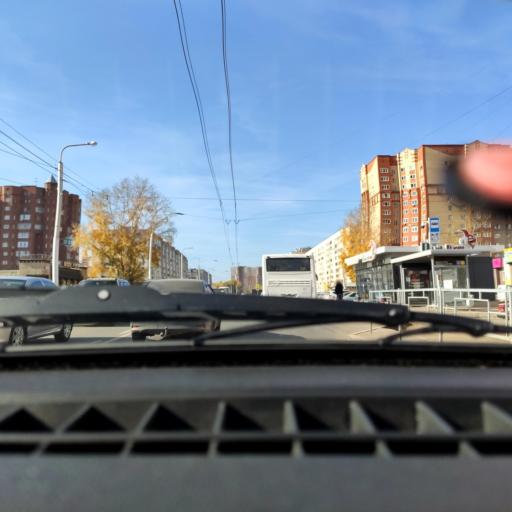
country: RU
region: Bashkortostan
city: Ufa
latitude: 54.7802
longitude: 56.1233
